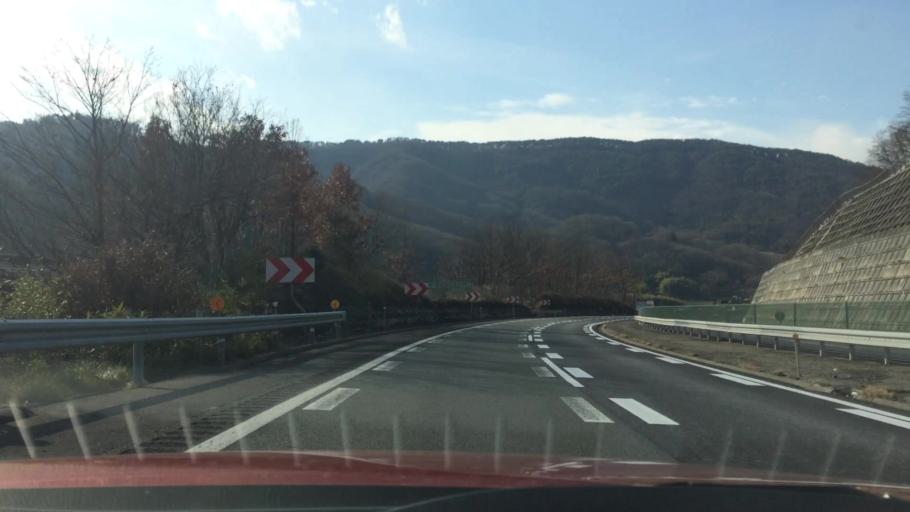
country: JP
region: Nagano
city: Toyoshina
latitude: 36.3448
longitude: 137.9603
